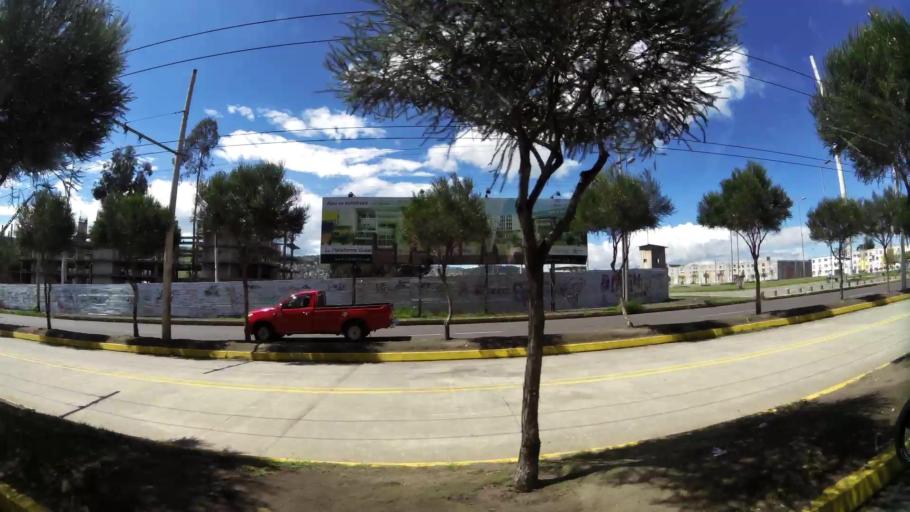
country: EC
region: Pichincha
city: Quito
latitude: -0.2932
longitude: -78.5474
